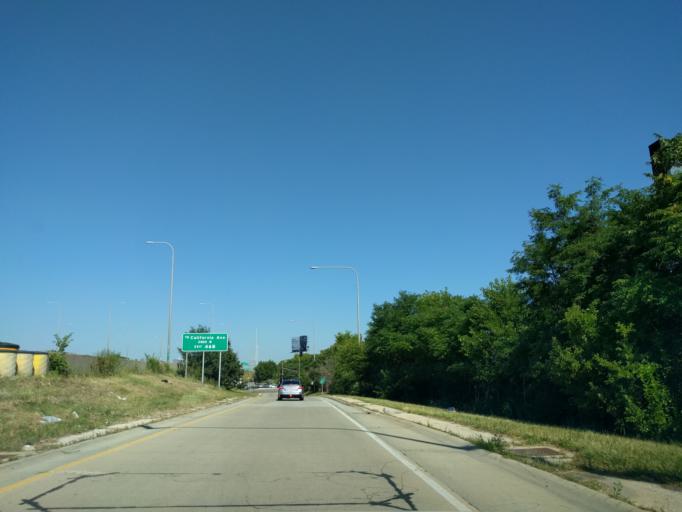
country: US
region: Illinois
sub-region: Cook County
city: Chicago
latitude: 41.9274
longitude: -87.6862
